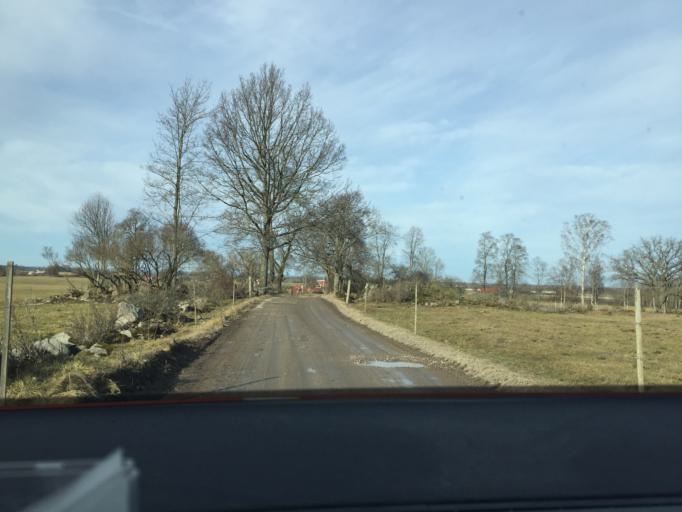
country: SE
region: OErebro
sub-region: Hallsbergs Kommun
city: Skollersta
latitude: 59.1229
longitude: 15.4344
